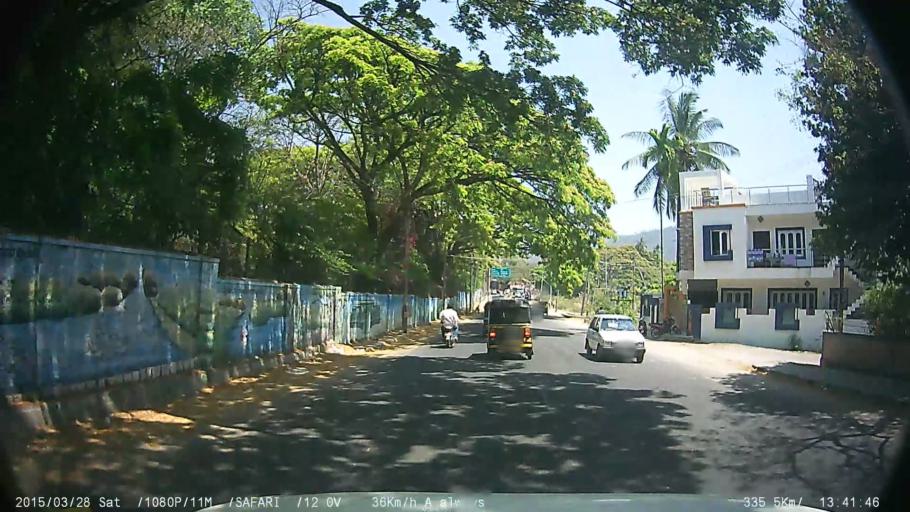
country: IN
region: Karnataka
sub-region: Mysore
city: Mysore
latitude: 12.3001
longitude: 76.6654
